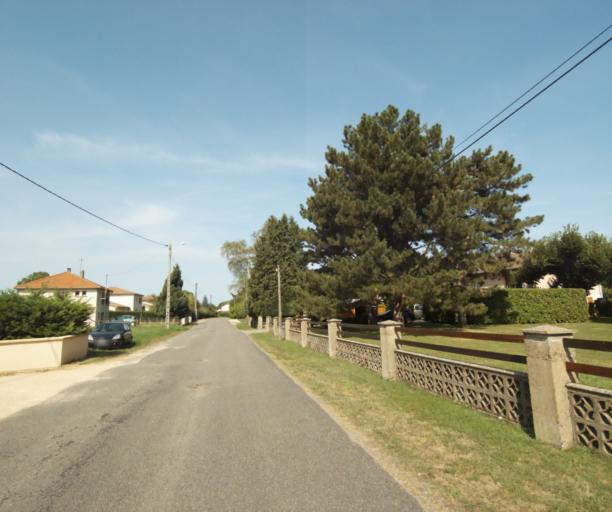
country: FR
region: Bourgogne
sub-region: Departement de Saone-et-Loire
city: Tournus
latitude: 46.5480
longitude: 4.8953
